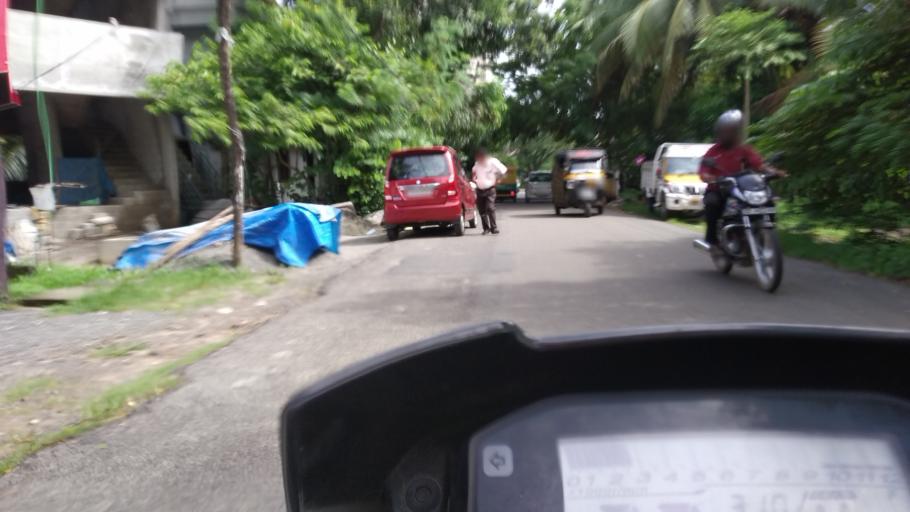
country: IN
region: Kerala
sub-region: Ernakulam
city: Cochin
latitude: 9.9865
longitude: 76.3030
